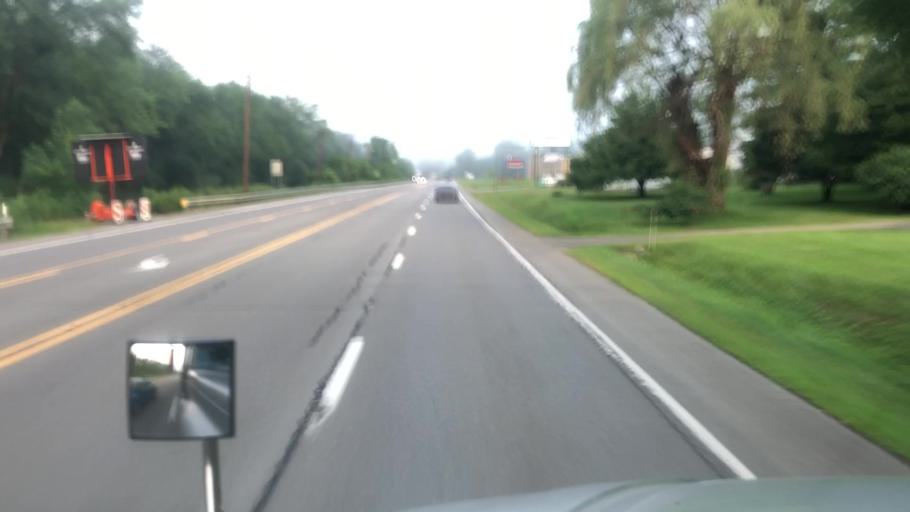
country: US
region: Pennsylvania
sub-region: Venango County
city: Woodland Heights
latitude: 41.4151
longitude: -79.7651
